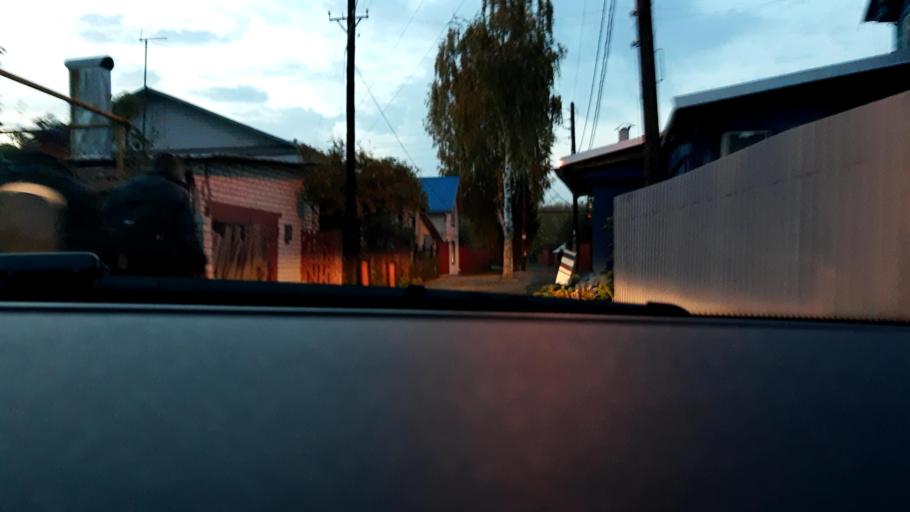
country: RU
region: Nizjnij Novgorod
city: Nizhniy Novgorod
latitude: 56.3340
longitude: 43.9137
